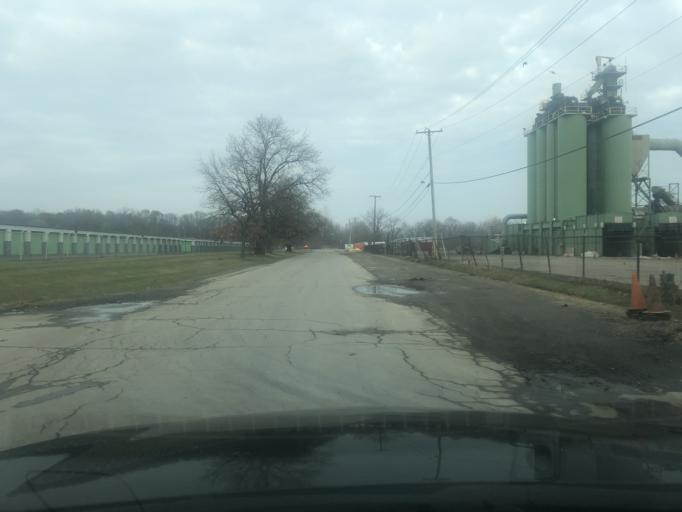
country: US
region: Michigan
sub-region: Wayne County
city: Belleville
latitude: 42.2199
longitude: -83.5420
